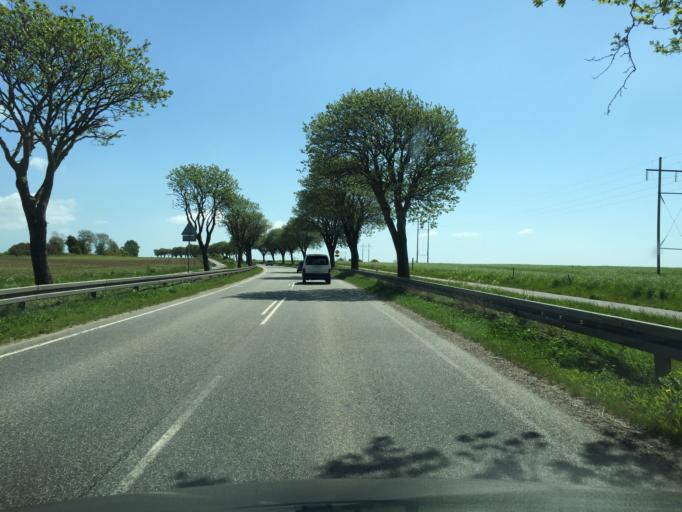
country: DK
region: Zealand
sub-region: Vordingborg Kommune
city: Stege
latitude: 54.9837
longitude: 12.1712
